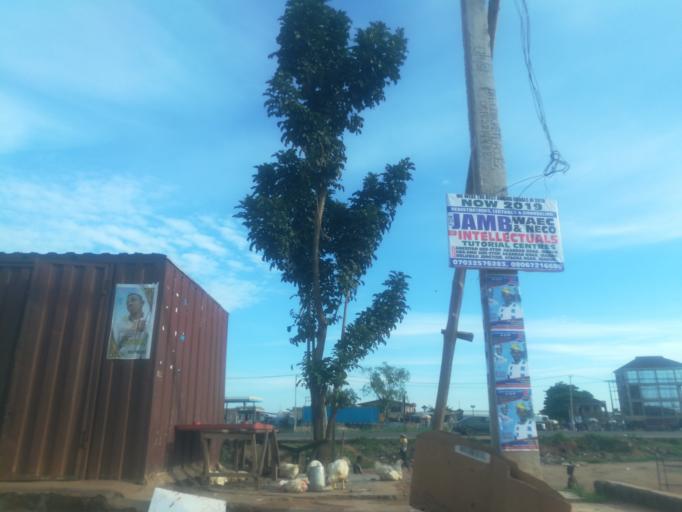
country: NG
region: Oyo
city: Ibadan
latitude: 7.3406
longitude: 3.9057
